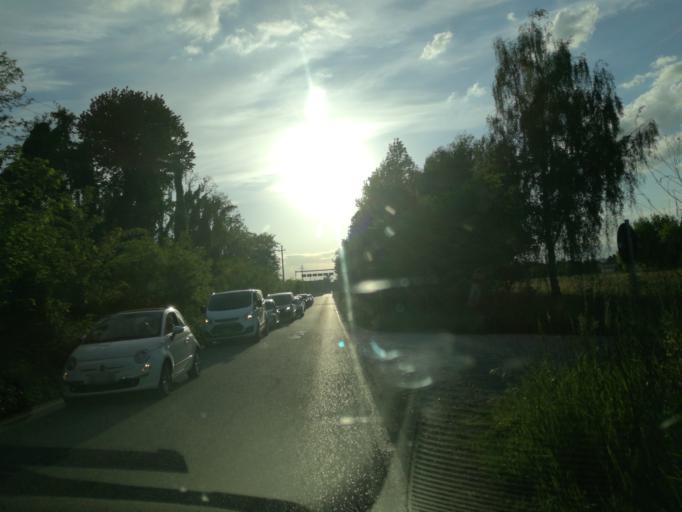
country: IT
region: Lombardy
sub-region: Provincia di Lecco
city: Merate
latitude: 45.6750
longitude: 9.4205
